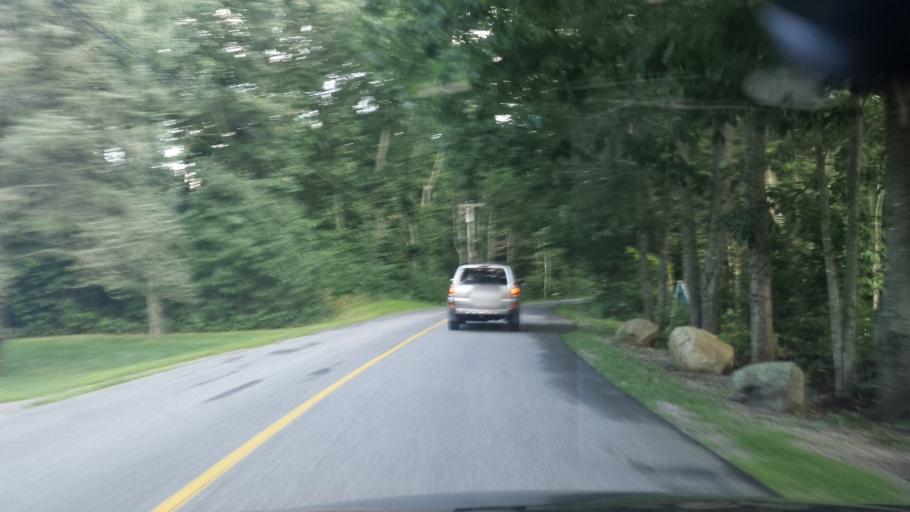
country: US
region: Maine
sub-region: York County
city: Arundel
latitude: 43.4280
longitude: -70.4515
